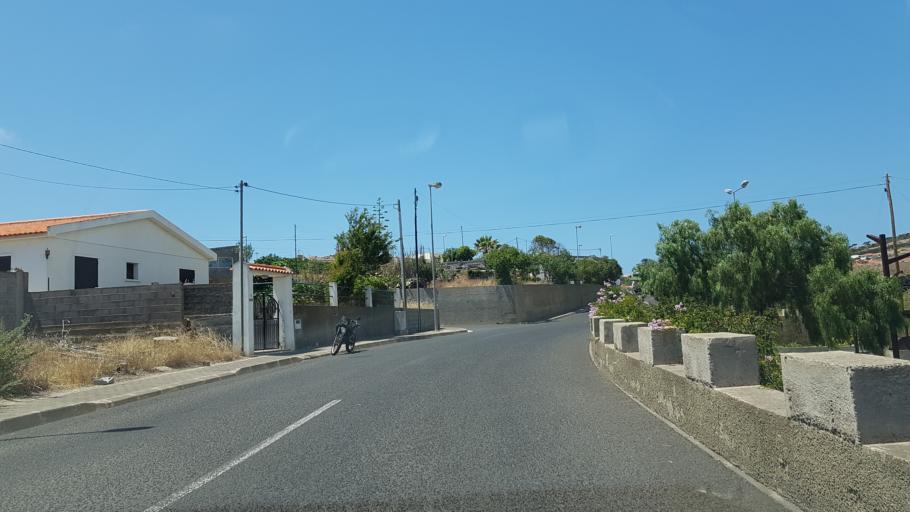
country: PT
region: Madeira
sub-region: Porto Santo
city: Vila de Porto Santo
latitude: 33.0670
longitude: -16.3415
